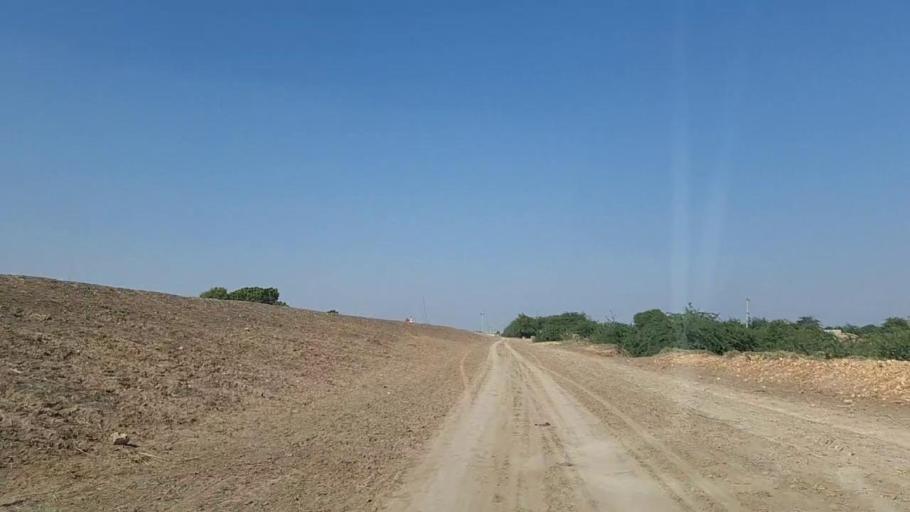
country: PK
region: Sindh
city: Chuhar Jamali
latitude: 24.5365
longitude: 68.0159
